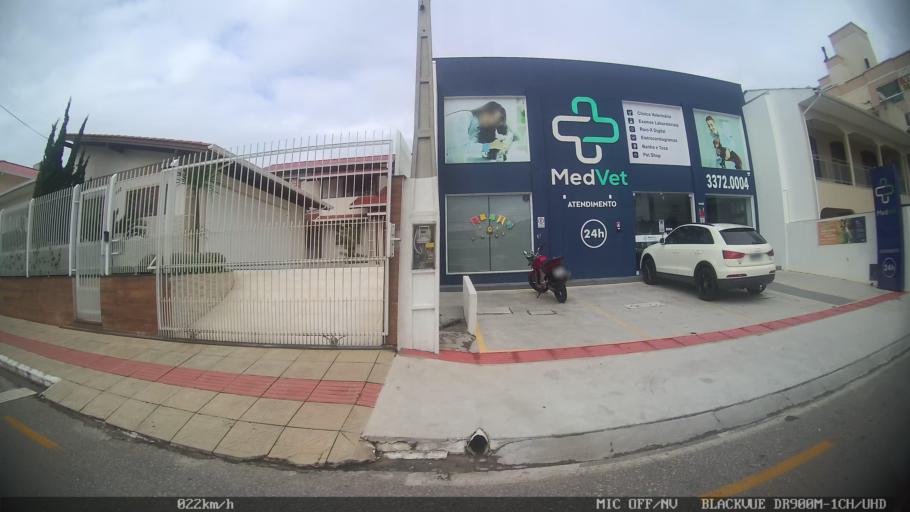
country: BR
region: Santa Catarina
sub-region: Sao Jose
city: Campinas
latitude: -27.5564
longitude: -48.6266
